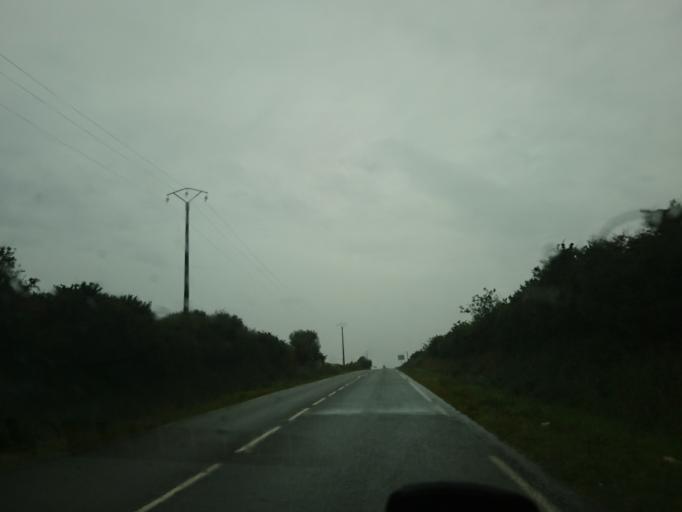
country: FR
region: Brittany
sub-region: Departement du Finistere
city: Plouguerneau
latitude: 48.6055
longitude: -4.4998
